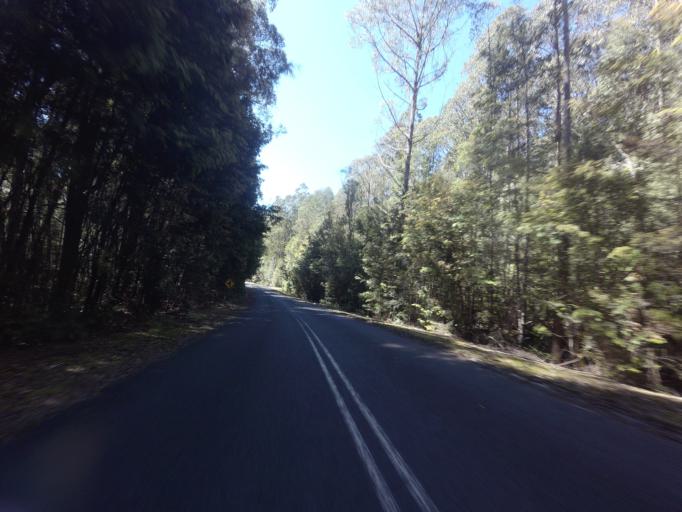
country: AU
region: Tasmania
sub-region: Huon Valley
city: Geeveston
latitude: -42.8227
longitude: 146.3329
